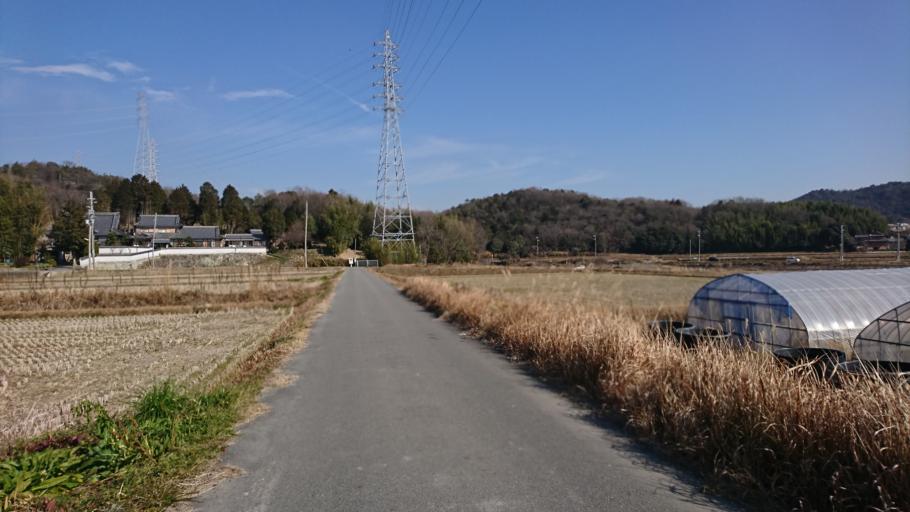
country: JP
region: Hyogo
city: Kakogawacho-honmachi
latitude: 34.8073
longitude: 134.8632
